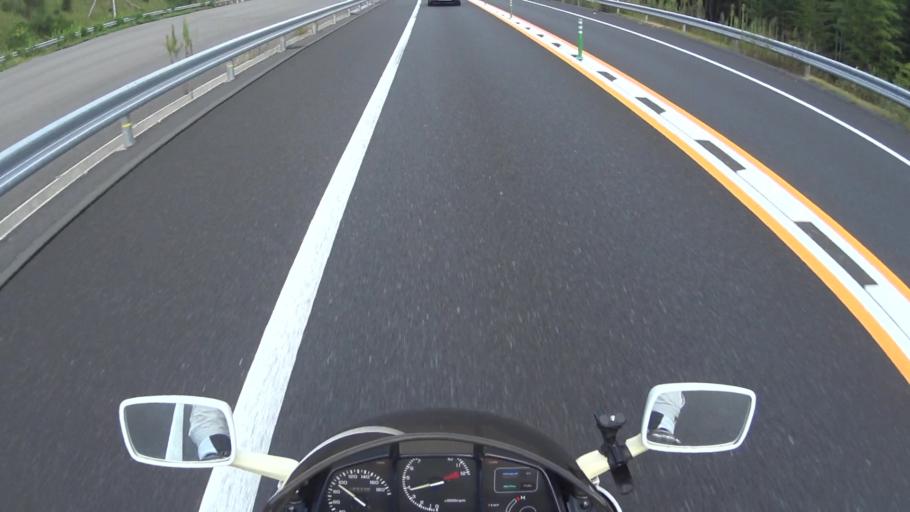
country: JP
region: Kyoto
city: Miyazu
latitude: 35.5507
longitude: 135.1405
